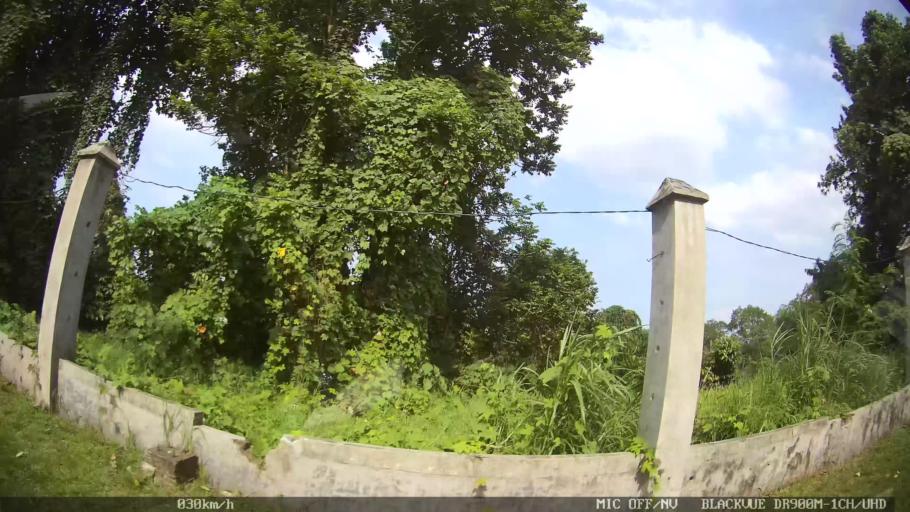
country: ID
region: North Sumatra
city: Medan
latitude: 3.5686
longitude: 98.6836
